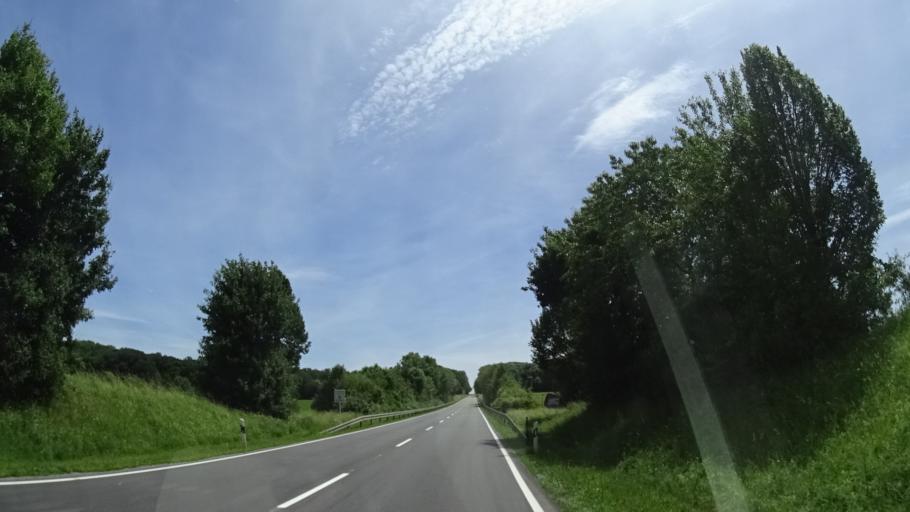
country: DE
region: Baden-Wuerttemberg
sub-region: Regierungsbezirk Stuttgart
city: Kupferzell
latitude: 49.1904
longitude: 9.6953
